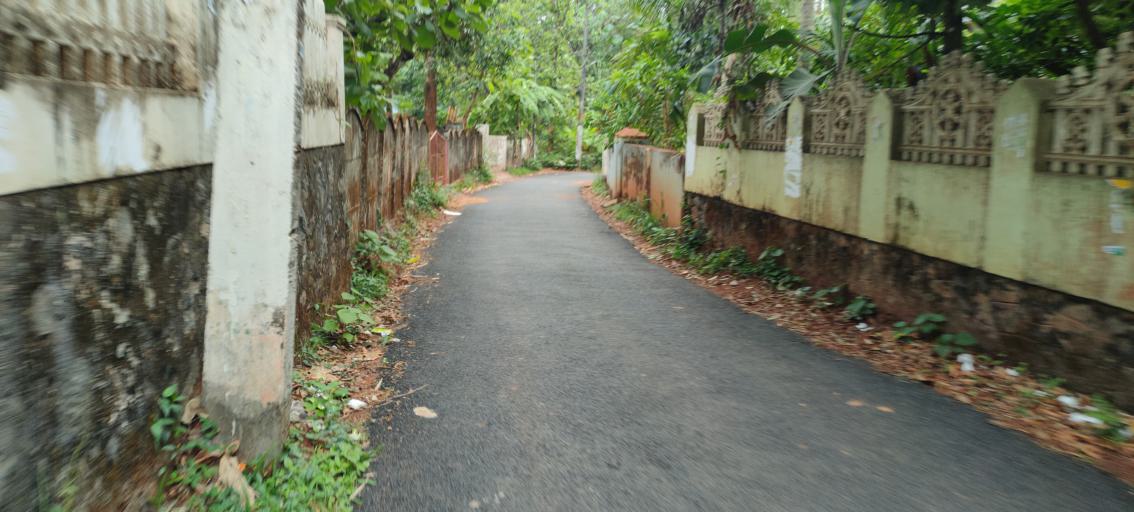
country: IN
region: Kerala
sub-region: Malappuram
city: Ponnani
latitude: 10.7750
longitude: 76.0314
